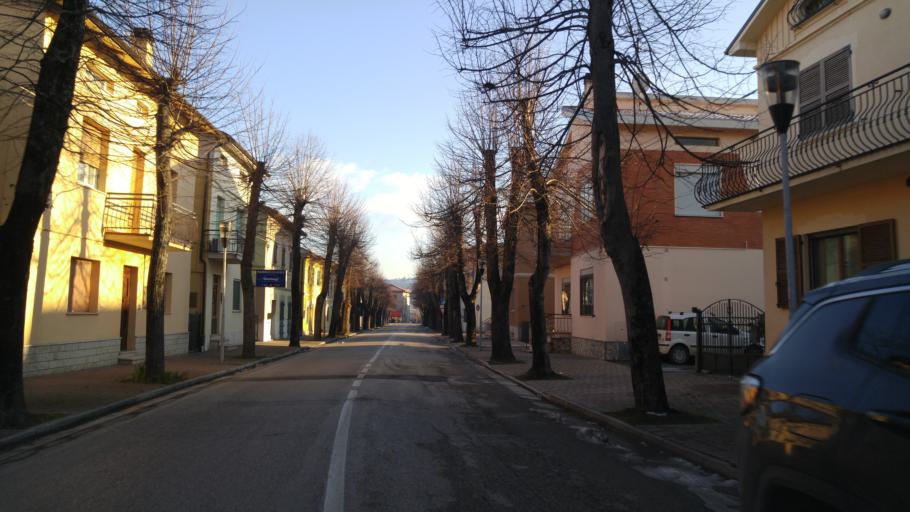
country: IT
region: The Marches
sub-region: Provincia di Pesaro e Urbino
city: San Michele
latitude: 43.6615
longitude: 12.9945
